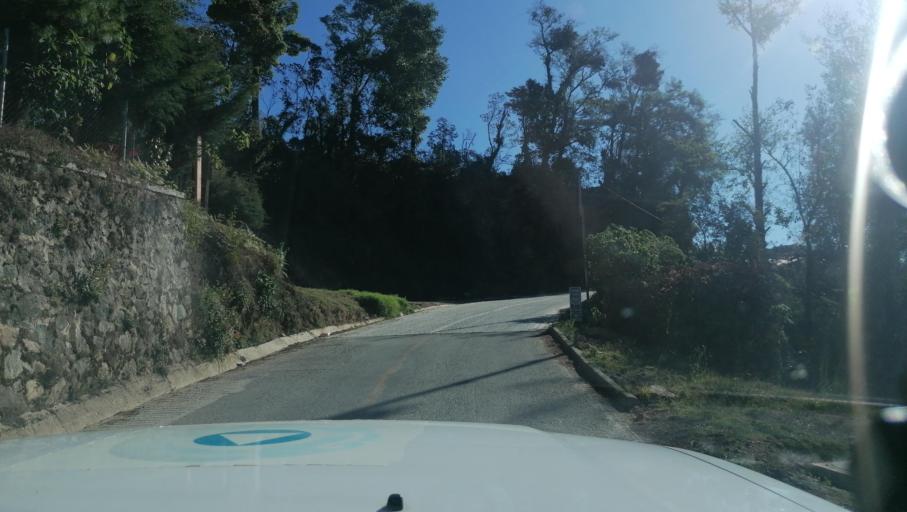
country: MX
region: Chiapas
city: Motozintla de Mendoza
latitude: 15.2559
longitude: -92.2140
